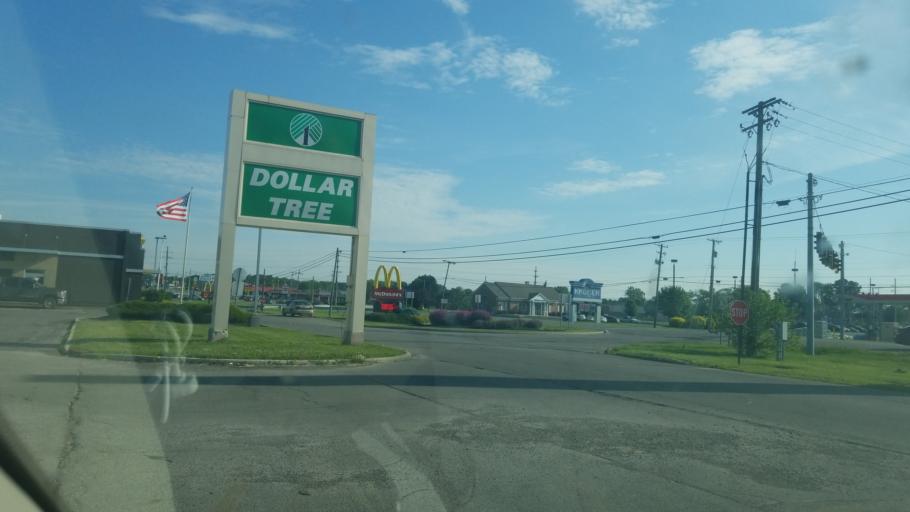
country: US
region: Ohio
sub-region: Marion County
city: Marion
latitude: 40.5620
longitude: -83.1197
